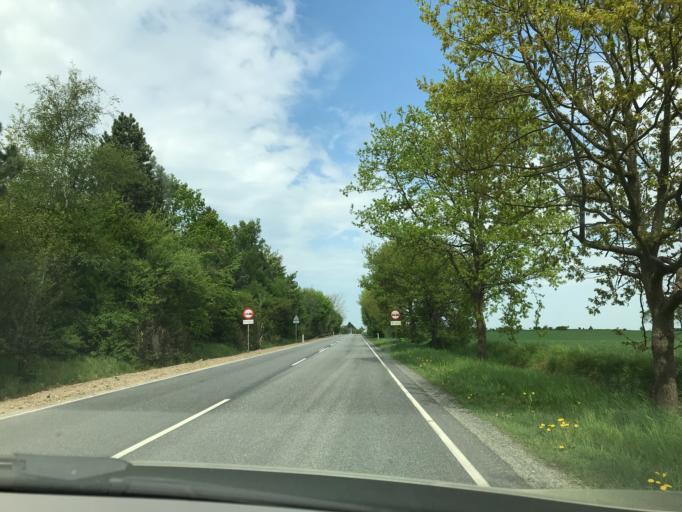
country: DK
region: South Denmark
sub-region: Assens Kommune
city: Assens
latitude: 55.2781
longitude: 9.9206
